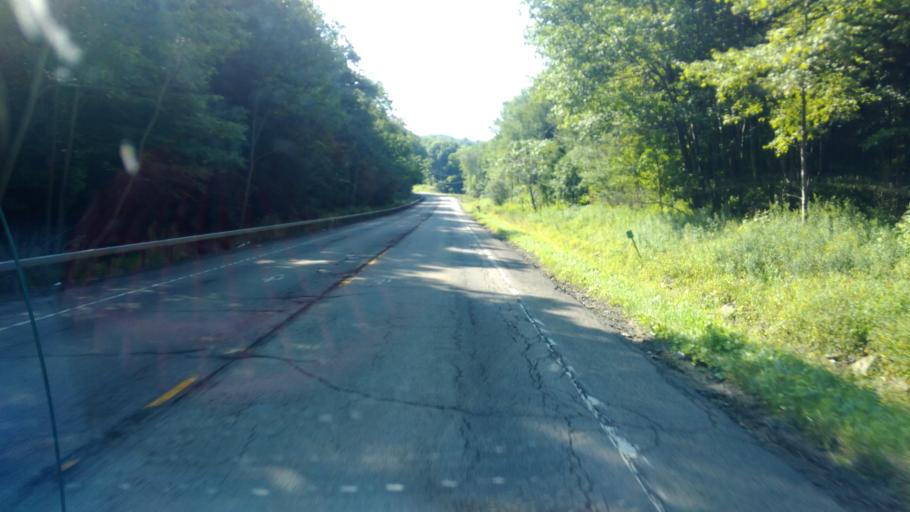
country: US
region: New York
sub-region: Allegany County
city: Cuba
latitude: 42.1799
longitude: -78.2558
